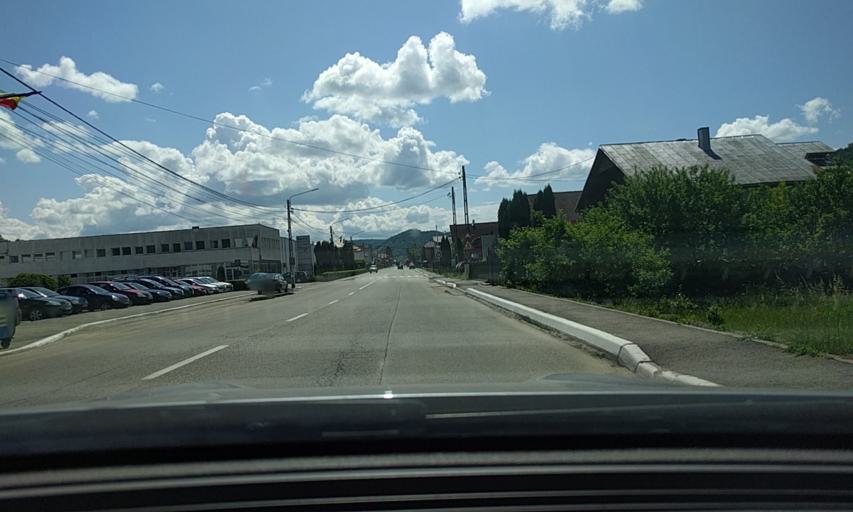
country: RO
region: Bistrita-Nasaud
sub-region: Oras Nasaud
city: Nasaud
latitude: 47.2957
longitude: 24.3819
